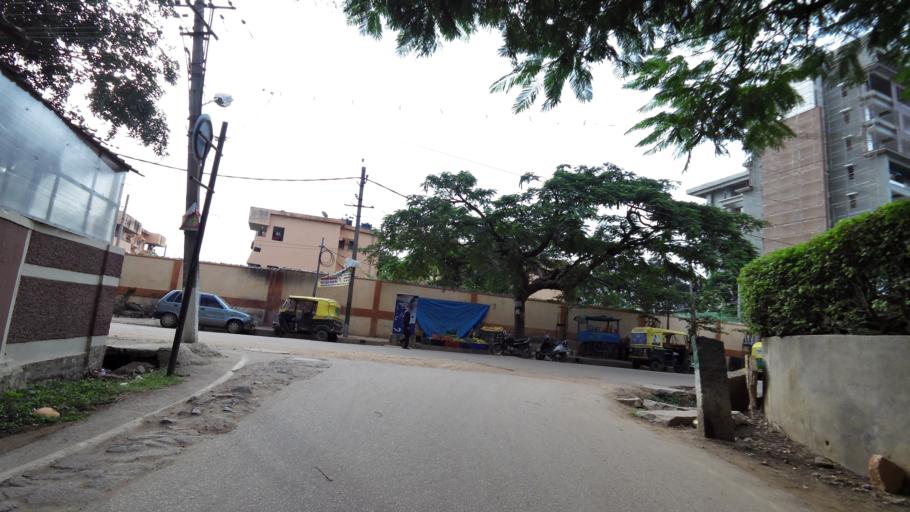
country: IN
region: Karnataka
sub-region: Bangalore Urban
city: Bangalore
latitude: 12.9995
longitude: 77.6287
